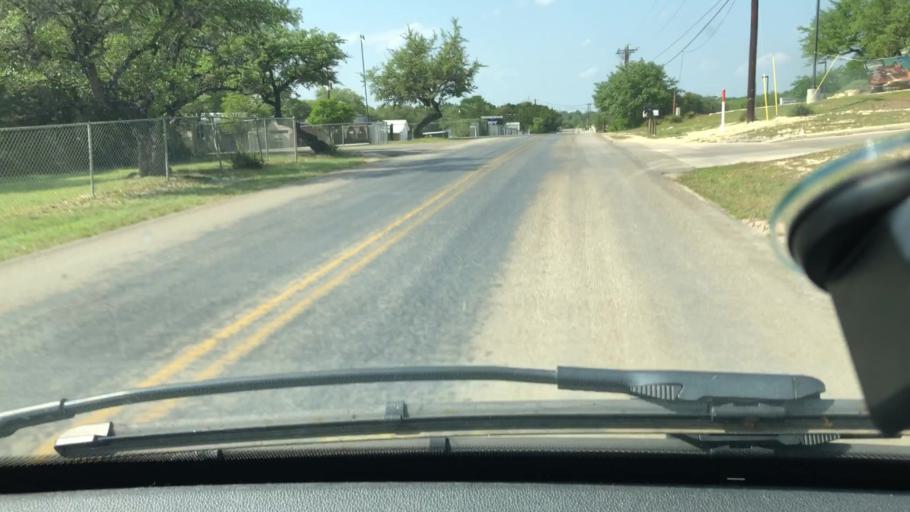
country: US
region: Texas
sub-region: Comal County
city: Bulverde
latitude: 29.7680
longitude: -98.4588
